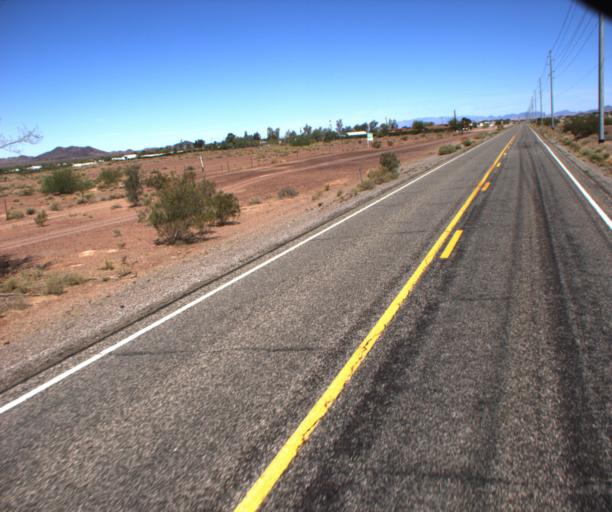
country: US
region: Arizona
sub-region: La Paz County
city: Quartzsite
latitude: 33.9149
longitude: -113.9922
